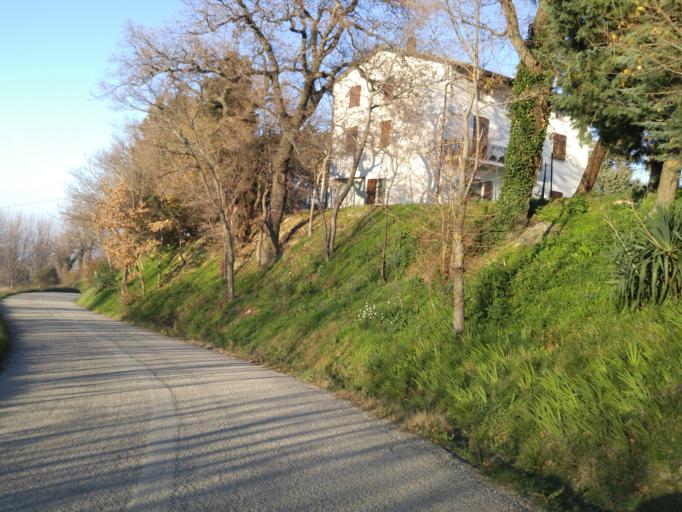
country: IT
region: The Marches
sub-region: Provincia di Pesaro e Urbino
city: Isola del Piano
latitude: 43.7318
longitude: 12.7568
